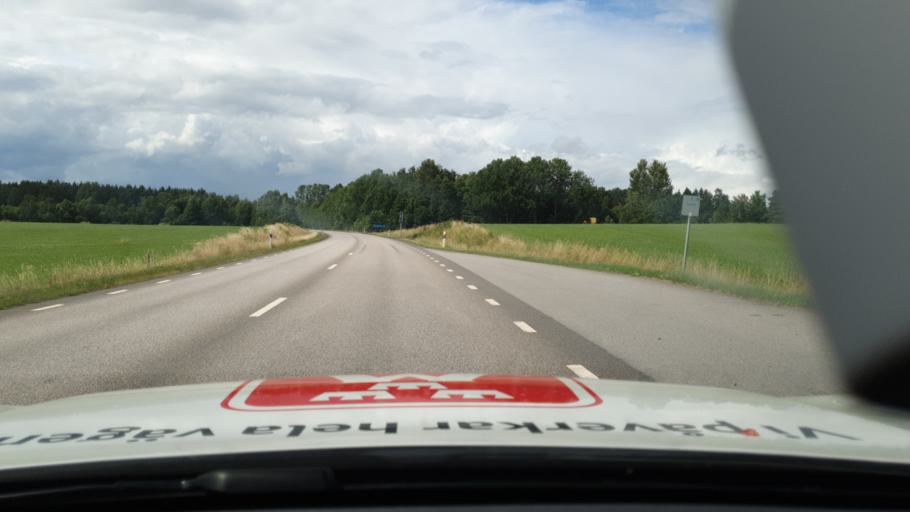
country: SE
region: Vaestra Goetaland
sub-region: Hjo Kommun
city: Hjo
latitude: 58.3325
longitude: 14.2530
